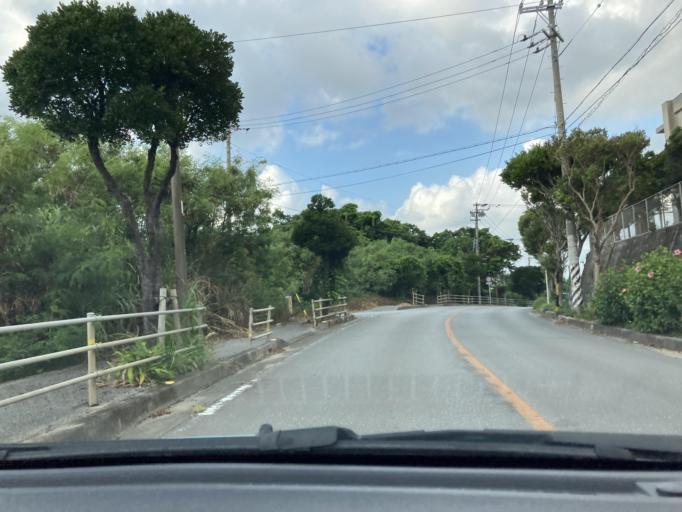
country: JP
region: Okinawa
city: Itoman
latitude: 26.0944
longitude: 127.6643
